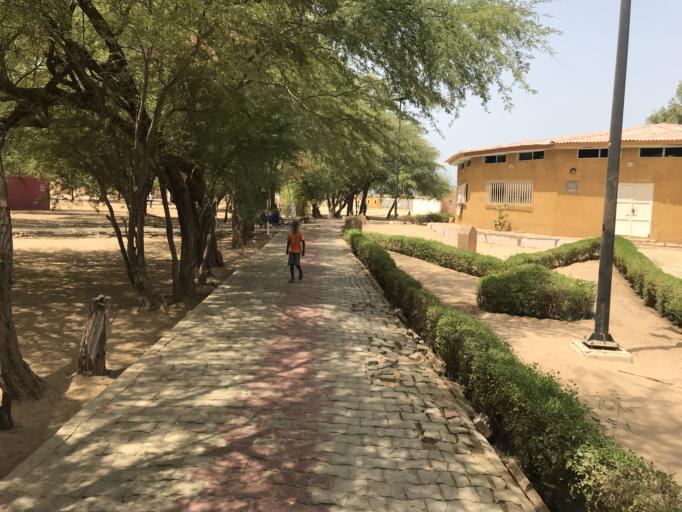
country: SN
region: Saint-Louis
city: Saint-Louis
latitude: 16.0651
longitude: -16.4253
